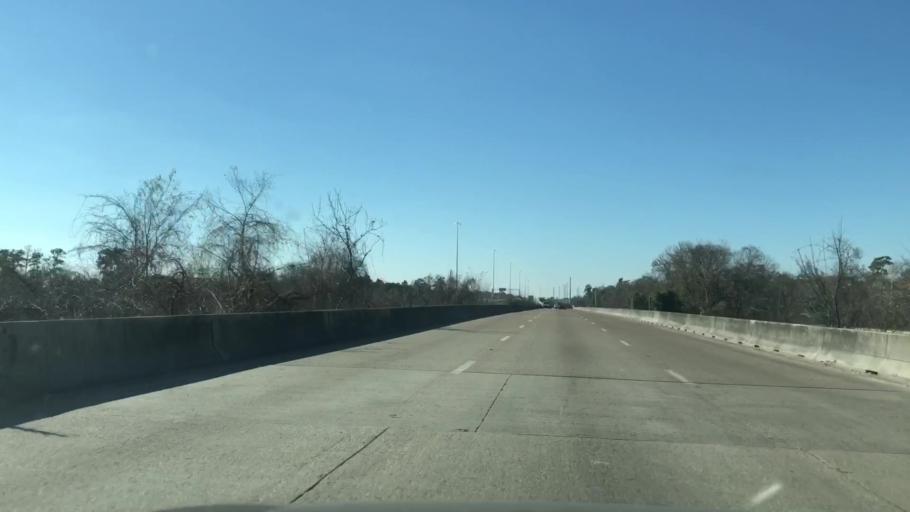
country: US
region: Texas
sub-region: Harris County
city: Jacinto City
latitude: 29.8112
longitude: -95.2126
